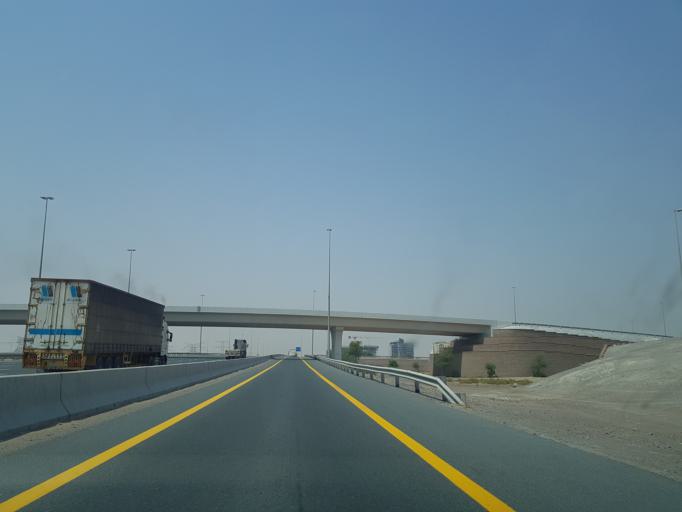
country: AE
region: Dubai
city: Dubai
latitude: 25.0896
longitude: 55.3949
